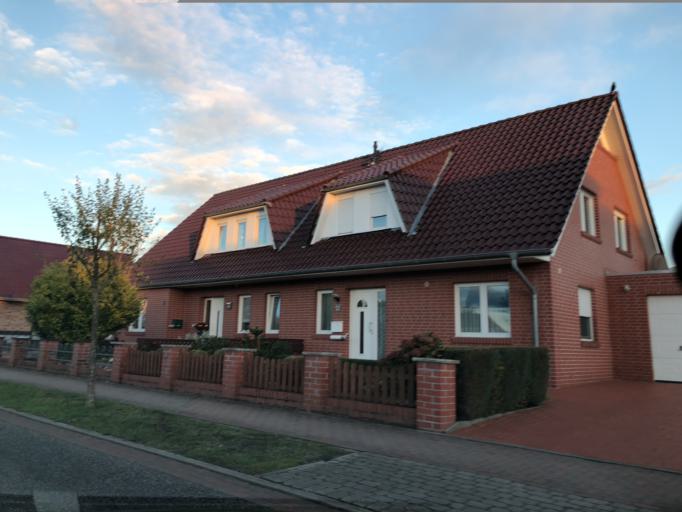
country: DE
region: Lower Saxony
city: Papenburg
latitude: 53.0854
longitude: 7.4182
